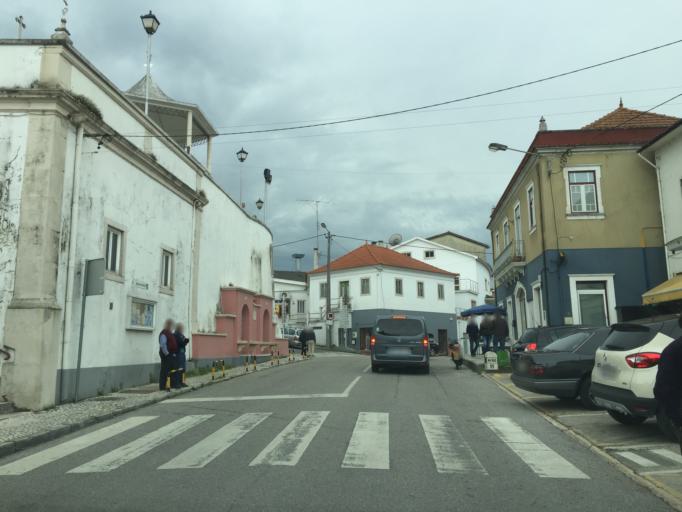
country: PT
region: Leiria
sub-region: Leiria
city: Caranguejeira
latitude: 39.7440
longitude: -8.7082
